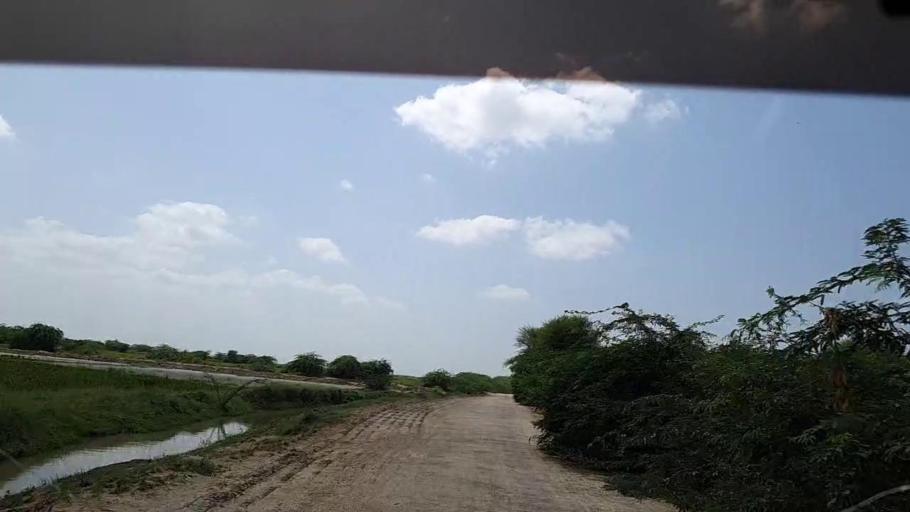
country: PK
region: Sindh
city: Badin
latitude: 24.5653
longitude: 68.7545
